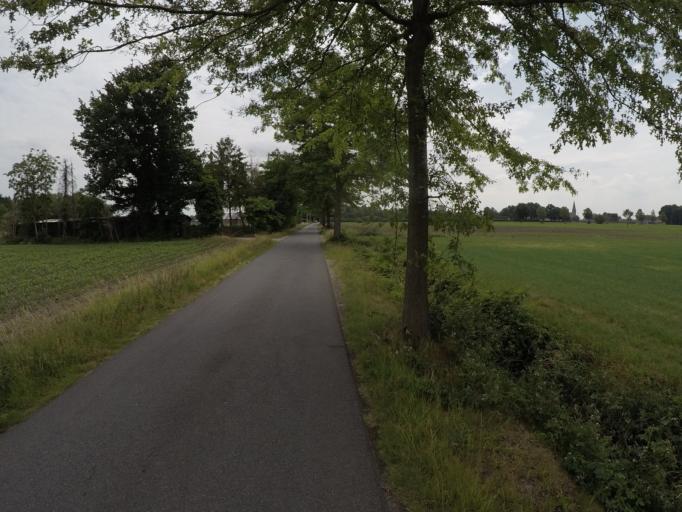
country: BE
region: Flanders
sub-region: Provincie Antwerpen
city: Essen
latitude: 51.4401
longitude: 4.5145
